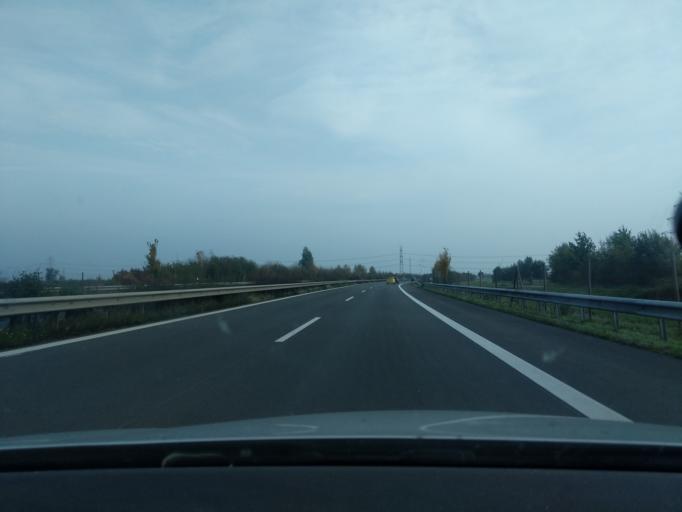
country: DE
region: Lower Saxony
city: Agathenburg
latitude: 53.5721
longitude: 9.5456
